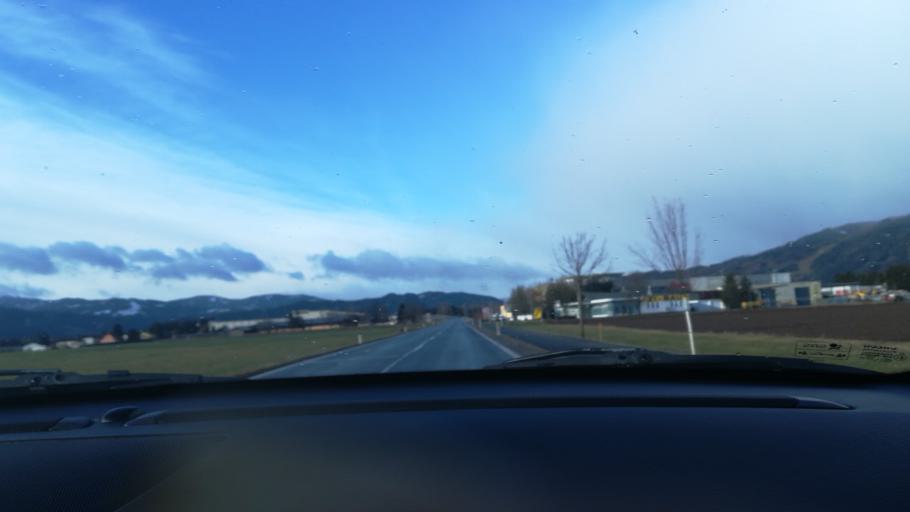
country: AT
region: Styria
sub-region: Politischer Bezirk Murtal
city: Zeltweg
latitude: 47.1950
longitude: 14.7360
